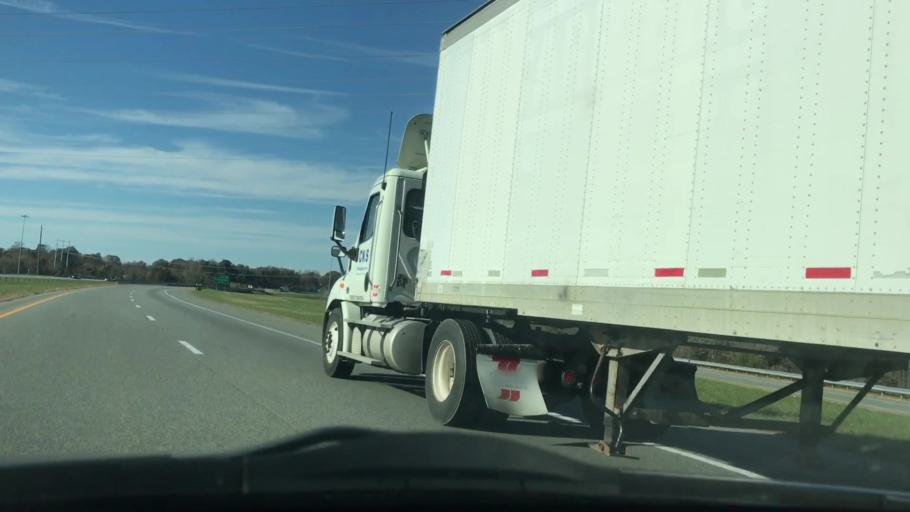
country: US
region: North Carolina
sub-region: Randolph County
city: Archdale
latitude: 35.9430
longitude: -79.9702
